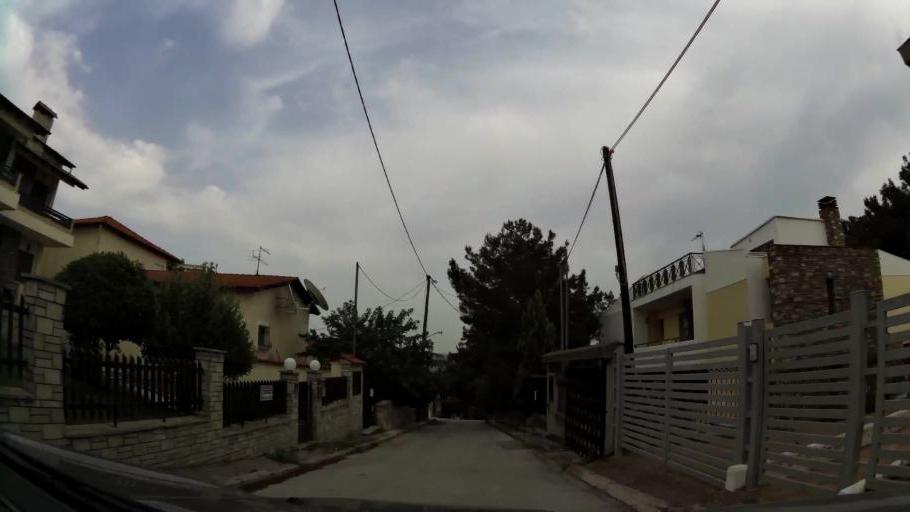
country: GR
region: Central Macedonia
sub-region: Nomos Thessalonikis
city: Oraiokastro
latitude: 40.7161
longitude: 22.9268
